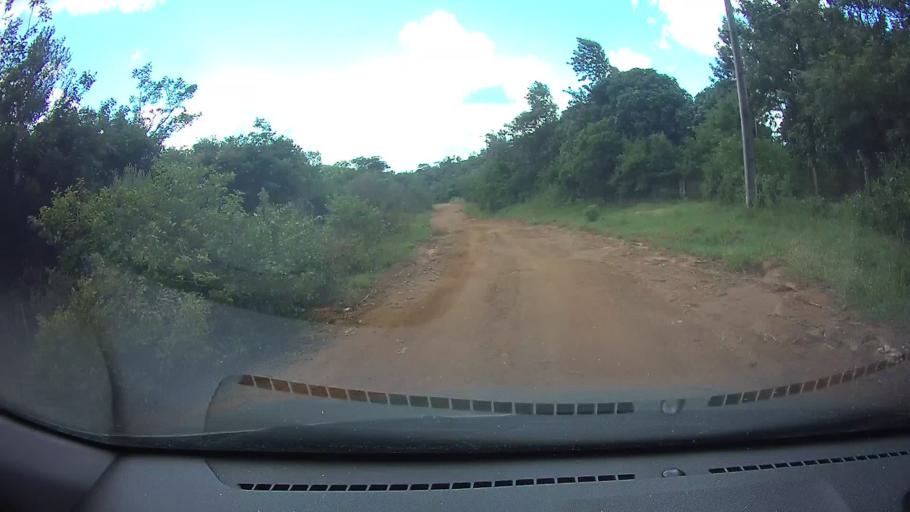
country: PY
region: Paraguari
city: La Colmena
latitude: -25.9323
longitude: -56.7838
